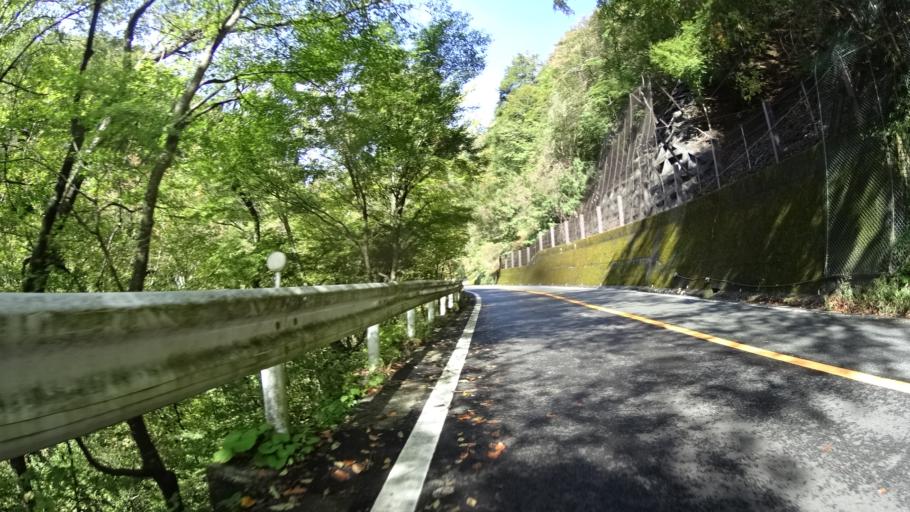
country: JP
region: Yamanashi
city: Enzan
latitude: 35.8045
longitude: 138.8503
